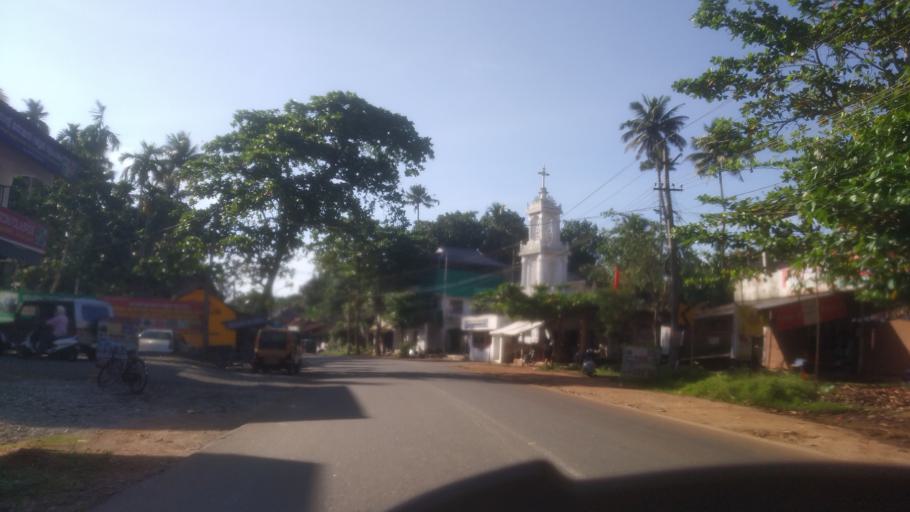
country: IN
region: Kerala
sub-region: Ernakulam
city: Ramamangalam
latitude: 9.9766
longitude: 76.4981
